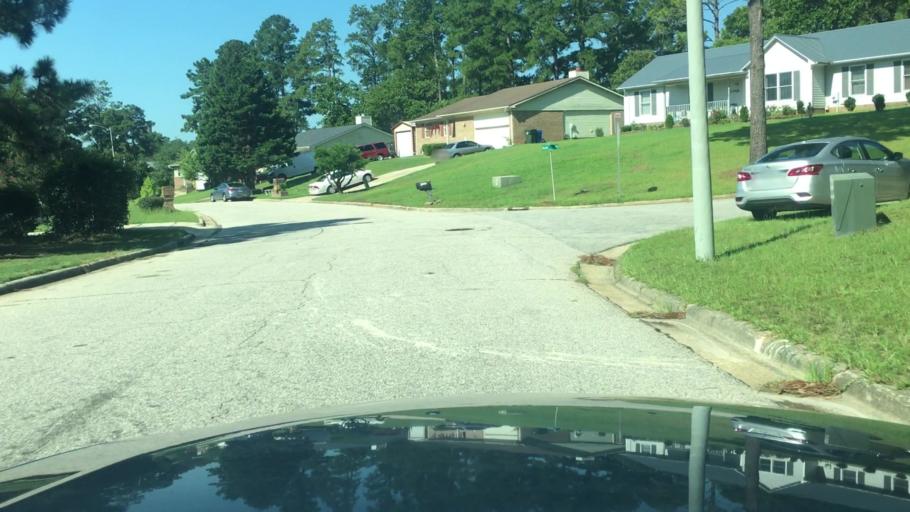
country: US
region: North Carolina
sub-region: Cumberland County
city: Fayetteville
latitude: 35.1079
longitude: -78.9062
